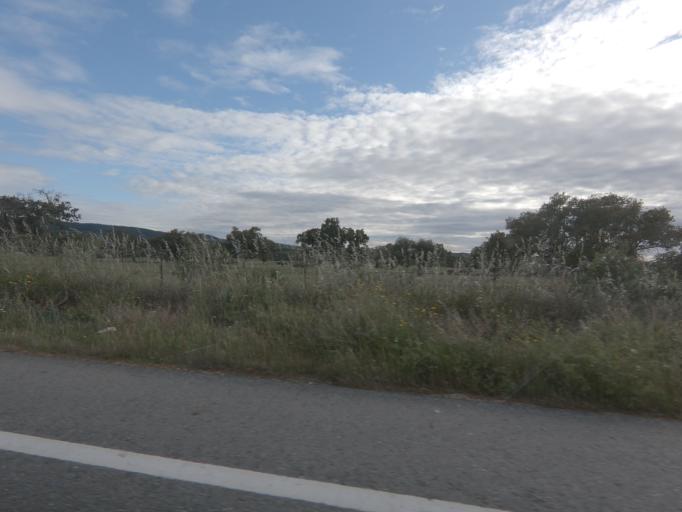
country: ES
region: Extremadura
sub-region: Provincia de Caceres
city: Pedroso de Acim
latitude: 39.8646
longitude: -6.4336
